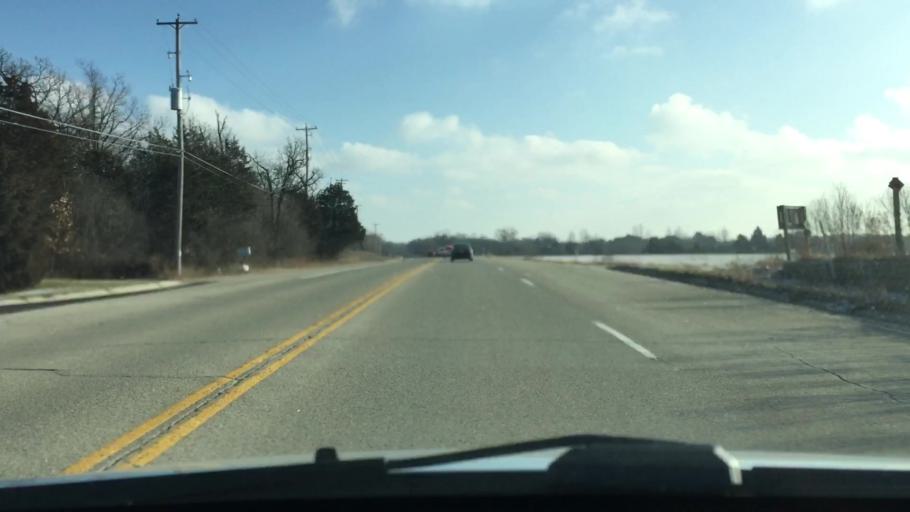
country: US
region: Wisconsin
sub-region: Waukesha County
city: Dousman
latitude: 43.0215
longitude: -88.4539
